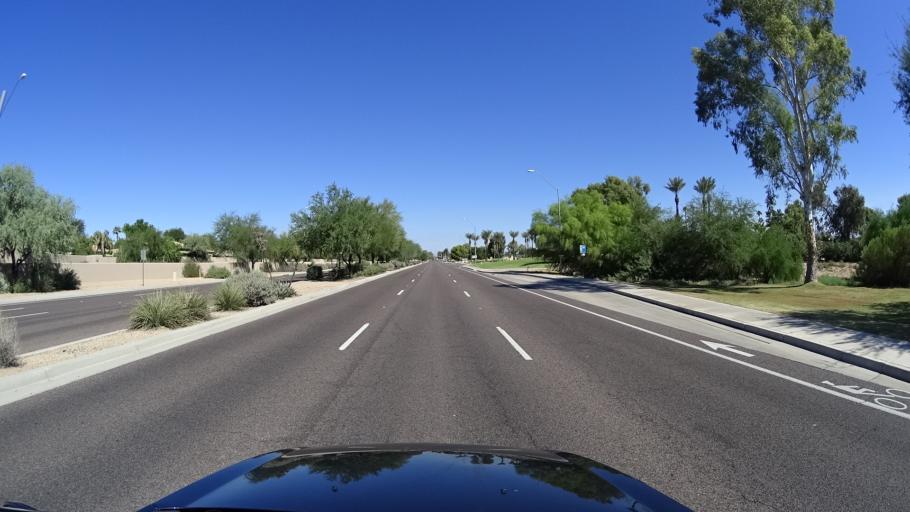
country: US
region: Arizona
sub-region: Maricopa County
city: Paradise Valley
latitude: 33.5464
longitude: -111.9258
